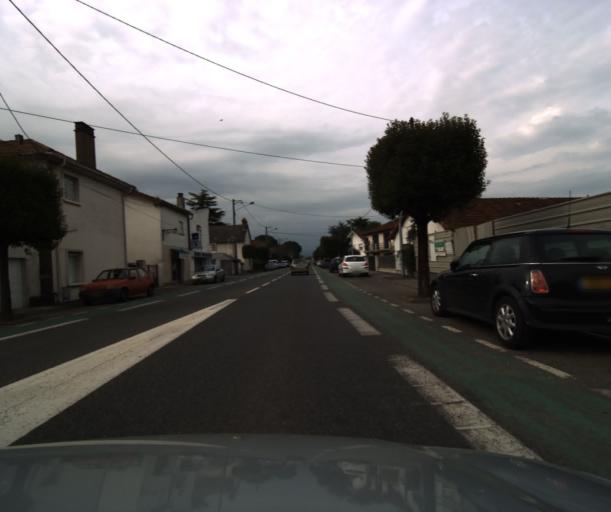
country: FR
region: Midi-Pyrenees
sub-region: Departement des Hautes-Pyrenees
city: Aureilhan
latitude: 43.2394
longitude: 0.0942
